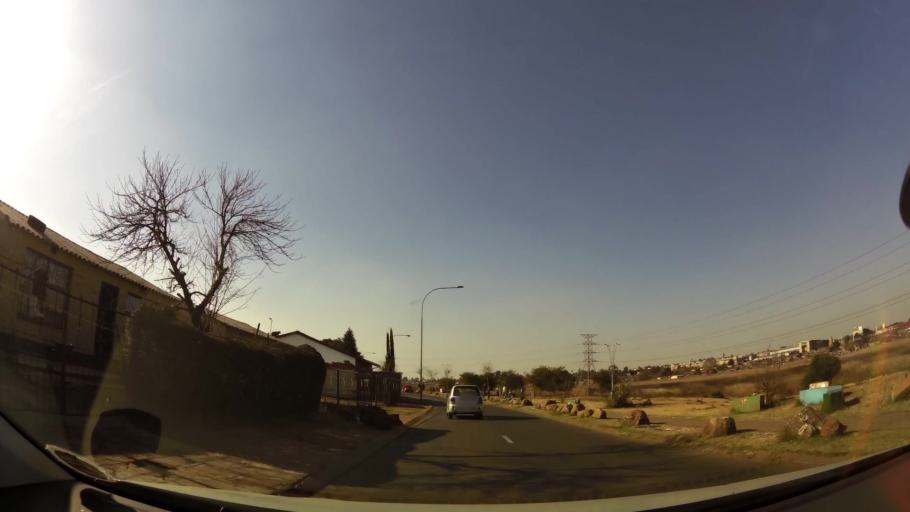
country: ZA
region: Gauteng
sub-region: City of Johannesburg Metropolitan Municipality
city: Soweto
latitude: -26.2774
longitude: 27.8801
